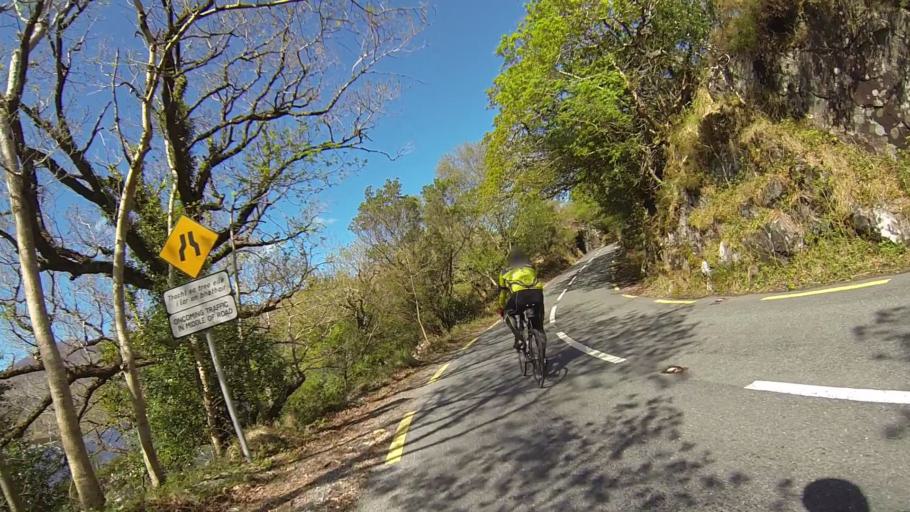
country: IE
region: Munster
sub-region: Ciarrai
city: Cill Airne
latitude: 51.9801
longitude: -9.5744
